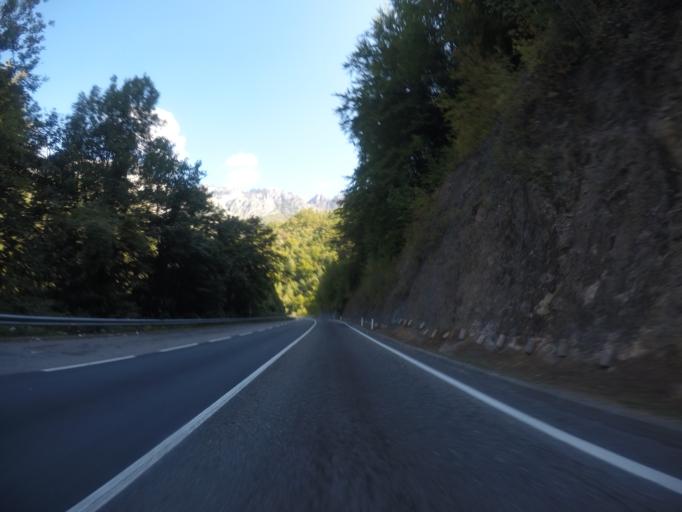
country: ME
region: Opstina Kolasin
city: Kolasin
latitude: 42.8148
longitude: 19.4017
